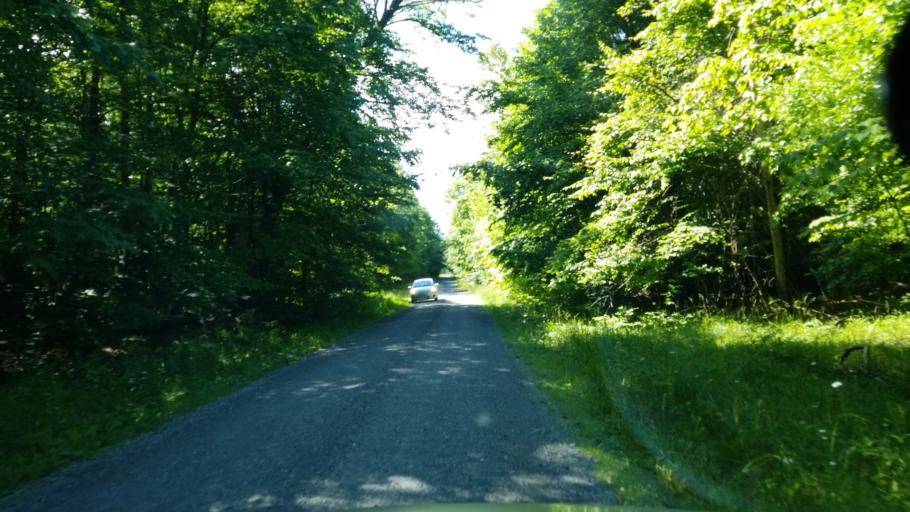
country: US
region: Pennsylvania
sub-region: Clearfield County
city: Clearfield
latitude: 41.2061
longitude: -78.4903
